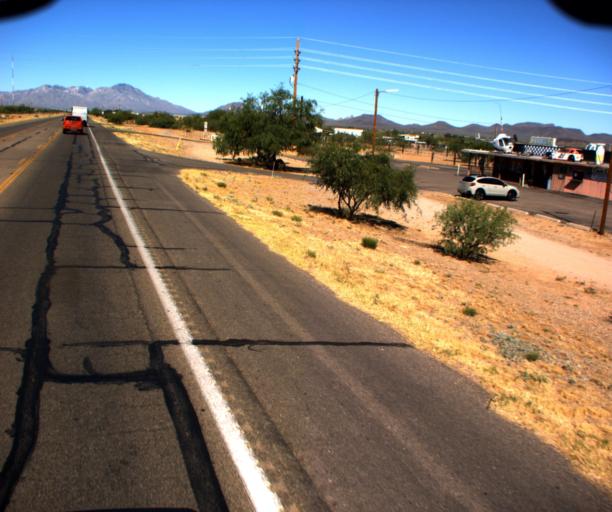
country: US
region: Arizona
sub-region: Pima County
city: Three Points
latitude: 32.0854
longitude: -111.2916
